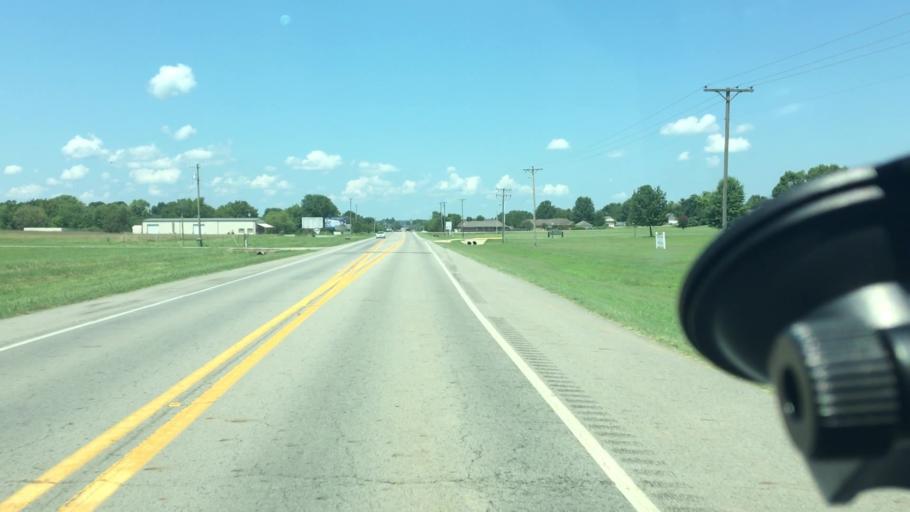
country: US
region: Arkansas
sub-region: Franklin County
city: Charleston
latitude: 35.2967
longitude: -94.0118
